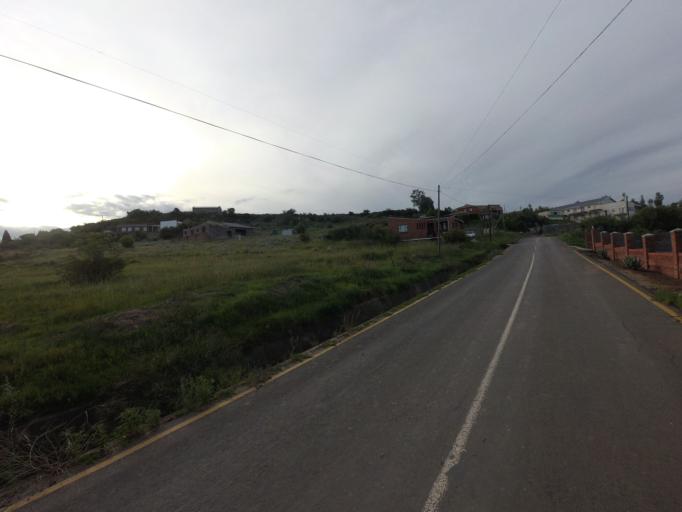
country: LS
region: Maseru
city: Maseru
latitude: -29.3063
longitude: 27.5074
